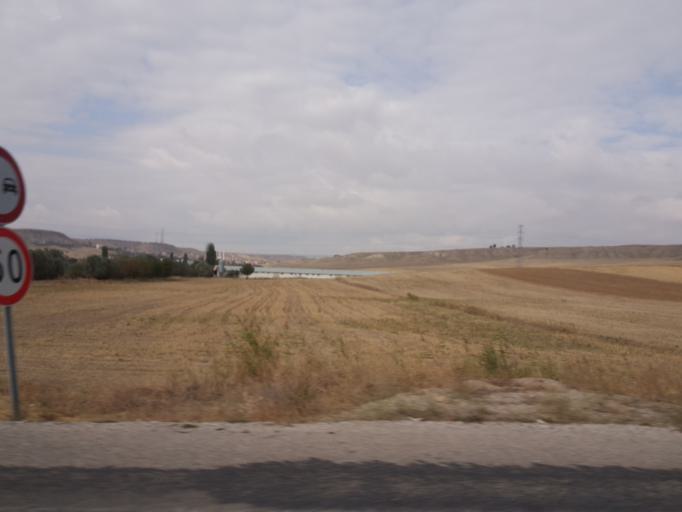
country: TR
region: Kirikkale
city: Karakecili
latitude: 39.5860
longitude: 33.4092
